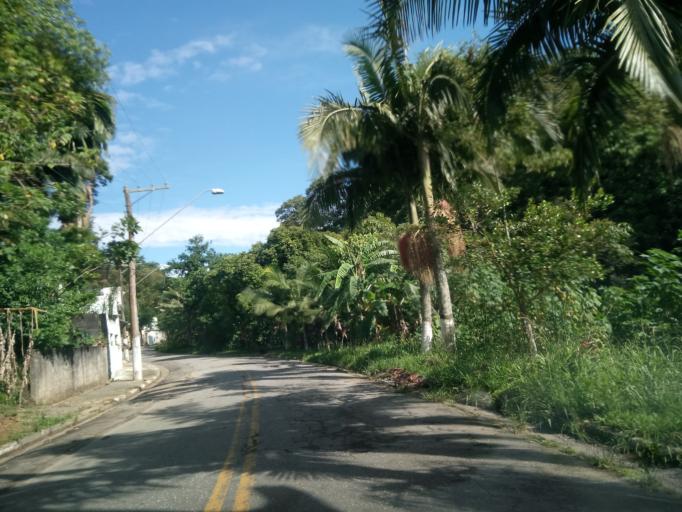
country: BR
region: Sao Paulo
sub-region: Sao Bernardo Do Campo
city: Sao Bernardo do Campo
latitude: -23.7992
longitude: -46.5324
